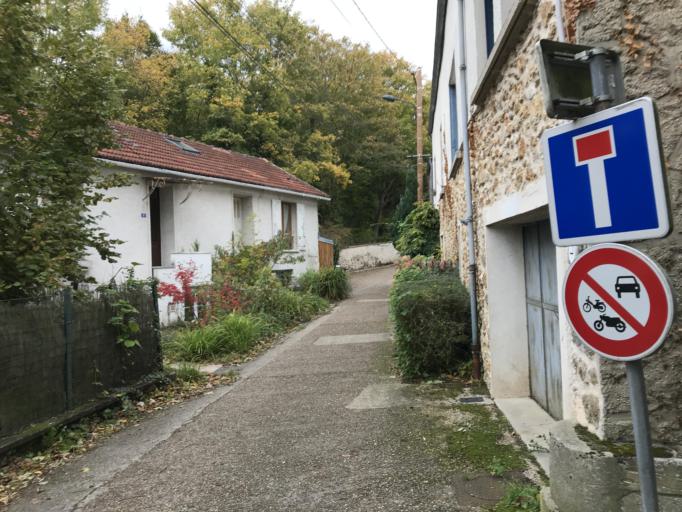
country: FR
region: Ile-de-France
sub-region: Departement de l'Essonne
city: Bures-sur-Yvette
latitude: 48.6941
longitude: 2.1590
